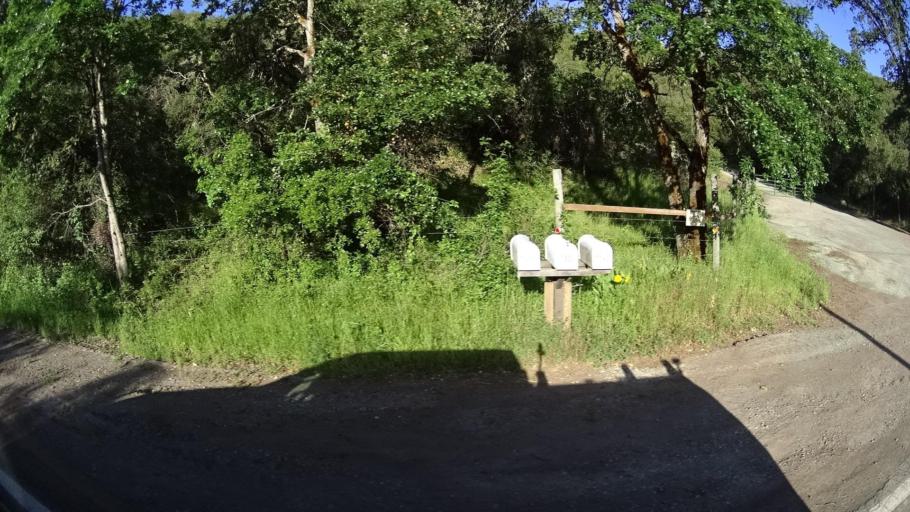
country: US
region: California
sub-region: Lake County
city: Upper Lake
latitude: 39.1373
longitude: -122.9996
